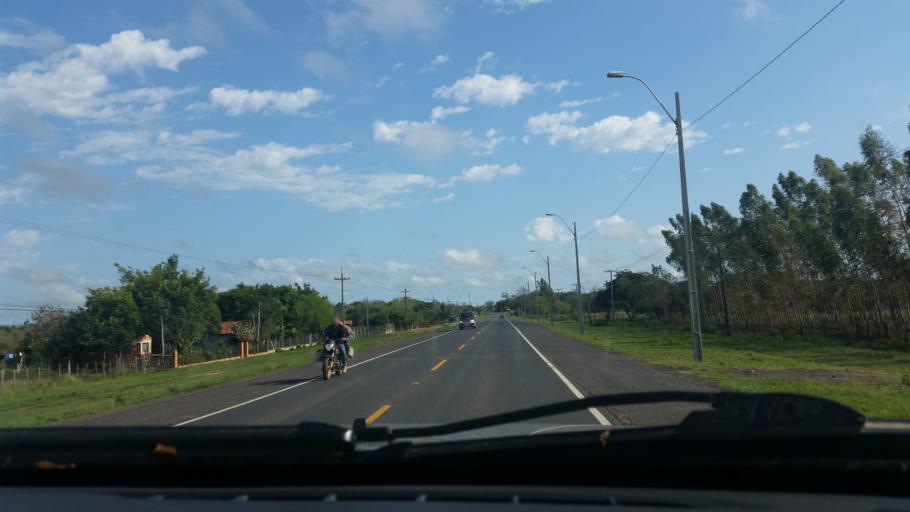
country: PY
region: Presidente Hayes
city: Benjamin Aceval
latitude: -25.0302
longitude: -57.5531
